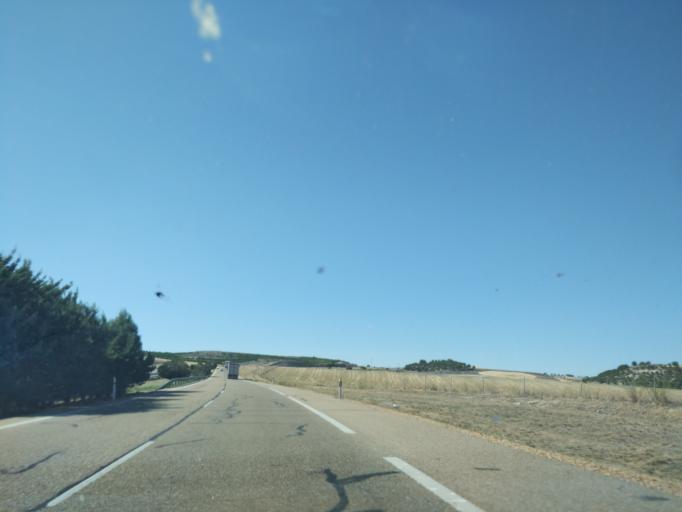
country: ES
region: Castille and Leon
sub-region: Provincia de Valladolid
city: Mota del Marques
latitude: 41.6564
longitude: -5.1930
